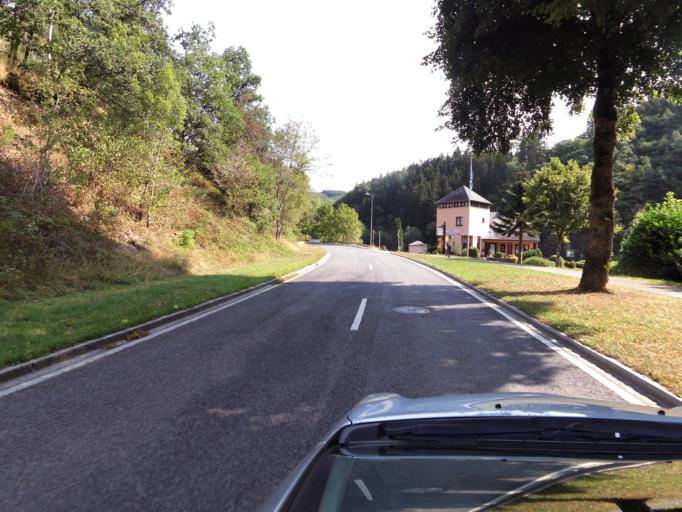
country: LU
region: Diekirch
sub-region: Canton de Wiltz
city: Esch-sur-Sure
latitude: 49.9068
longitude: 5.9419
